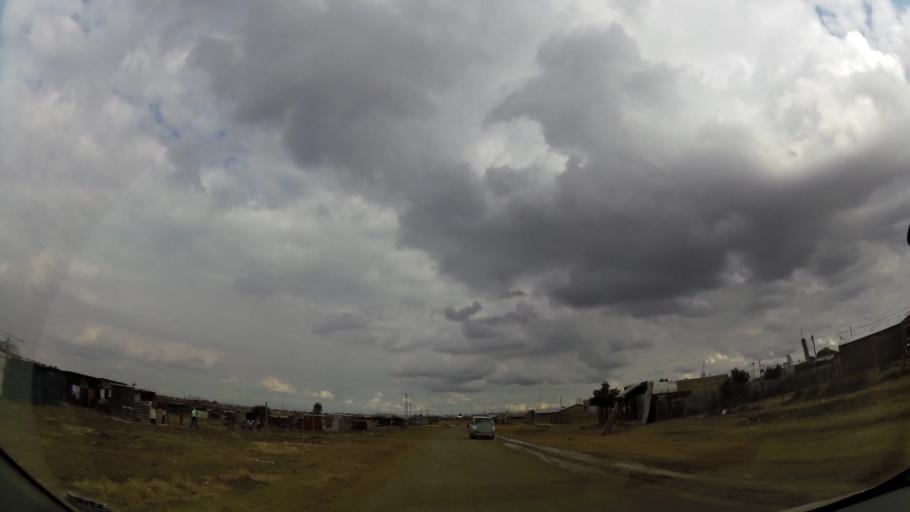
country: ZA
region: Orange Free State
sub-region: Fezile Dabi District Municipality
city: Sasolburg
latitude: -26.8716
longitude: 27.8734
